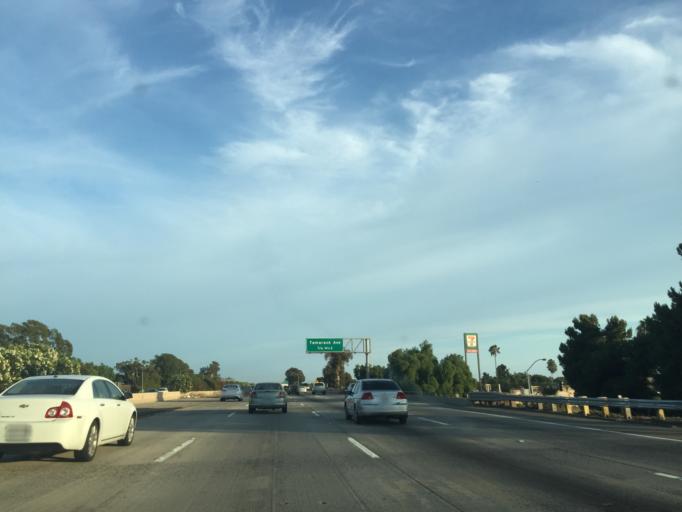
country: US
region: California
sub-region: San Diego County
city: Carlsbad
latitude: 33.1639
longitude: -117.3428
